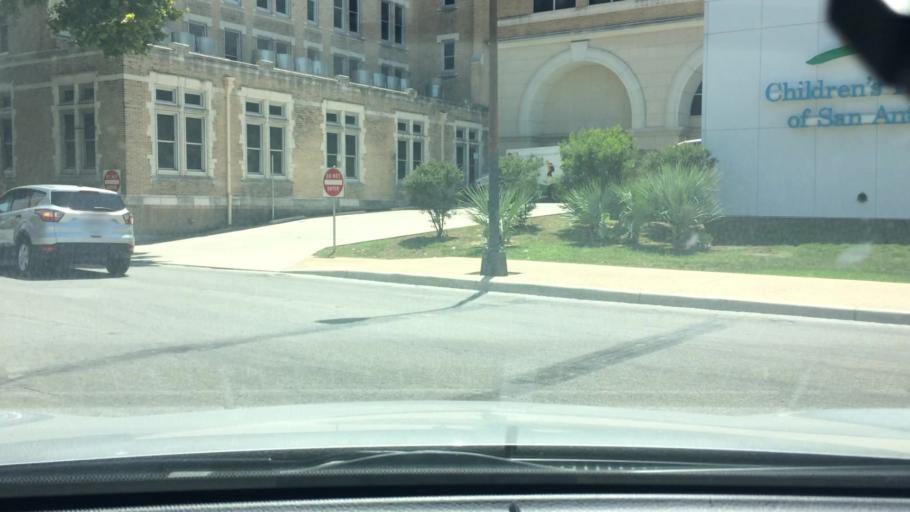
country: US
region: Texas
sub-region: Bexar County
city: San Antonio
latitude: 29.4274
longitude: -98.4979
